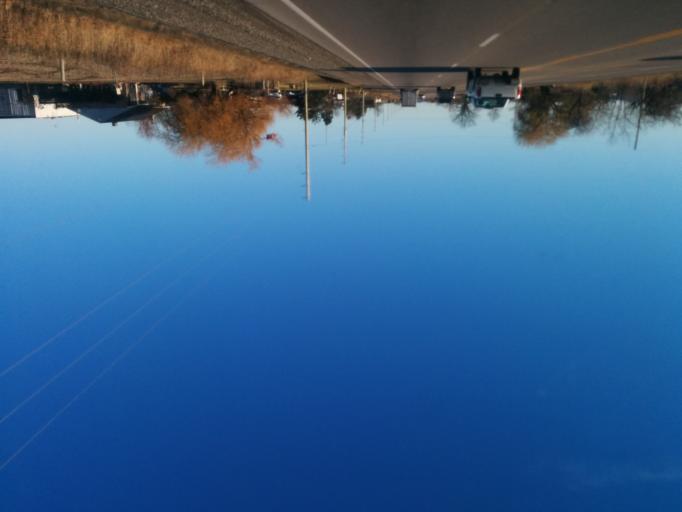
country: CA
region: Ontario
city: Brampton
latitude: 43.7645
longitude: -79.8661
